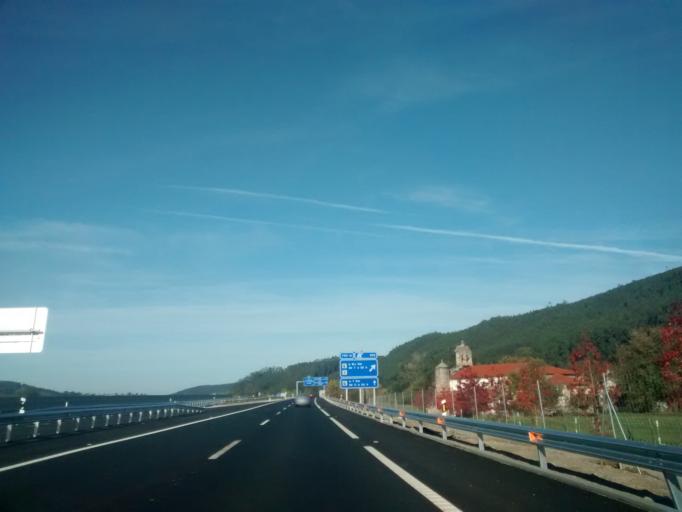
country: ES
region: Cantabria
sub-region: Provincia de Cantabria
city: Puente Viesgo
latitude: 43.3253
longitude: -3.9587
